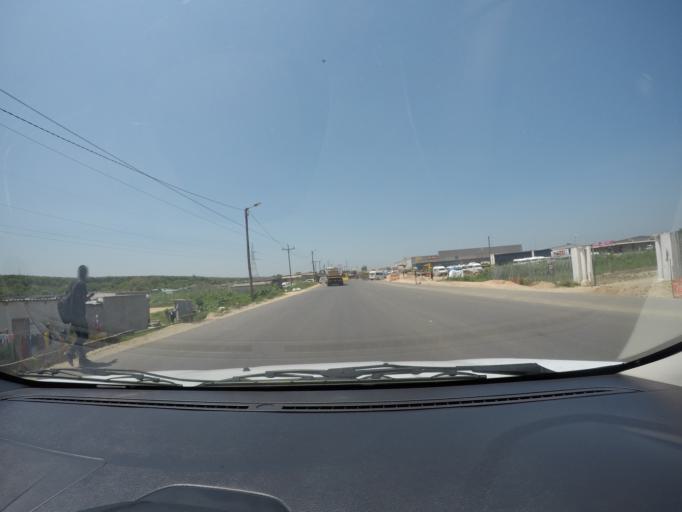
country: ZA
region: KwaZulu-Natal
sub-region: uThungulu District Municipality
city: eSikhawini
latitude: -28.8734
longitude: 31.8976
